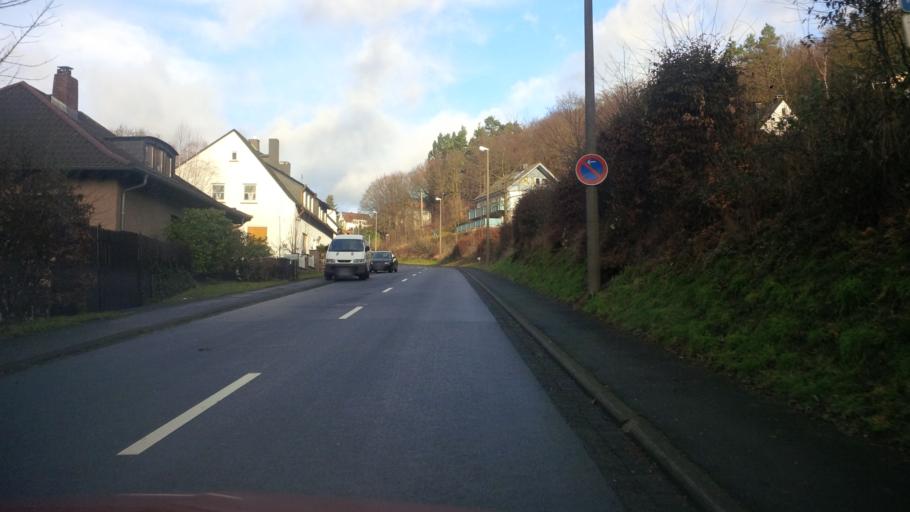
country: DE
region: Hesse
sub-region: Regierungsbezirk Darmstadt
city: Schmitten
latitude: 50.3143
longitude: 8.4259
